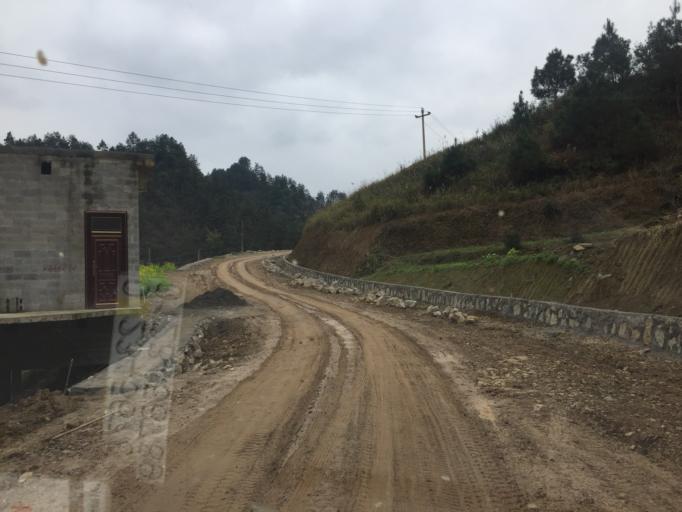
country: CN
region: Guizhou Sheng
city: Fuxing
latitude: 28.0699
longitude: 107.9116
